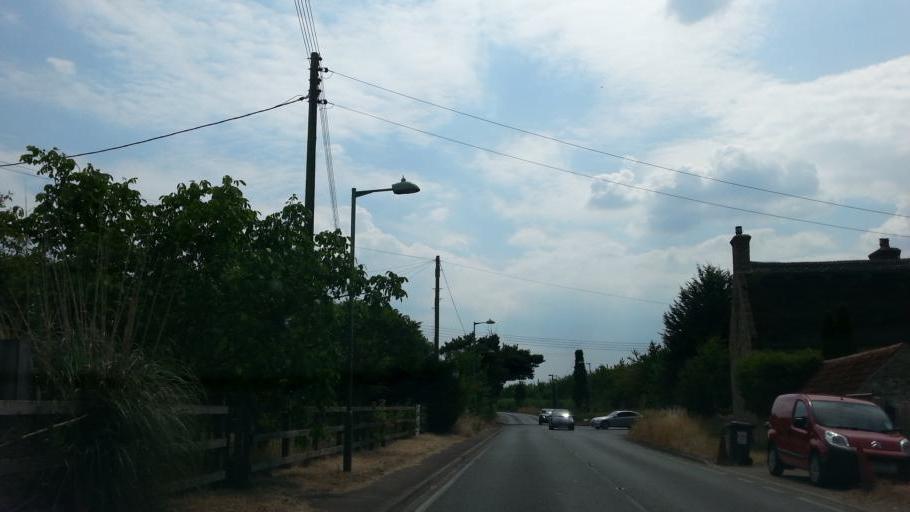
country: GB
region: England
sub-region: Suffolk
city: Lakenheath
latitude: 52.3815
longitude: 0.5267
